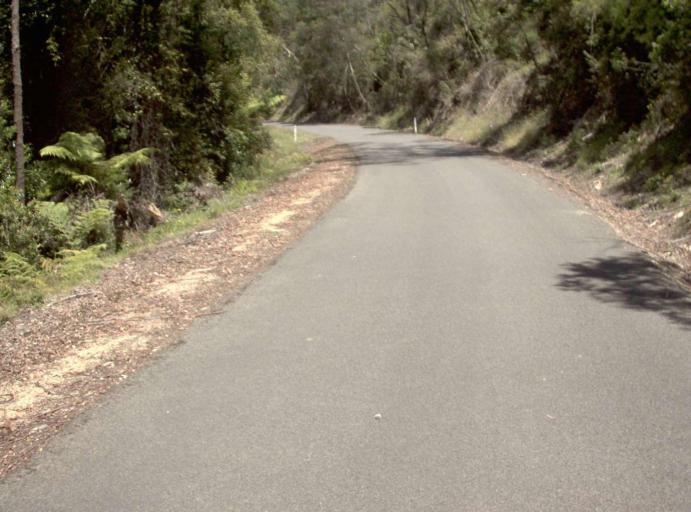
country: AU
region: New South Wales
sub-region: Bombala
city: Bombala
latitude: -37.4793
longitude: 148.9242
